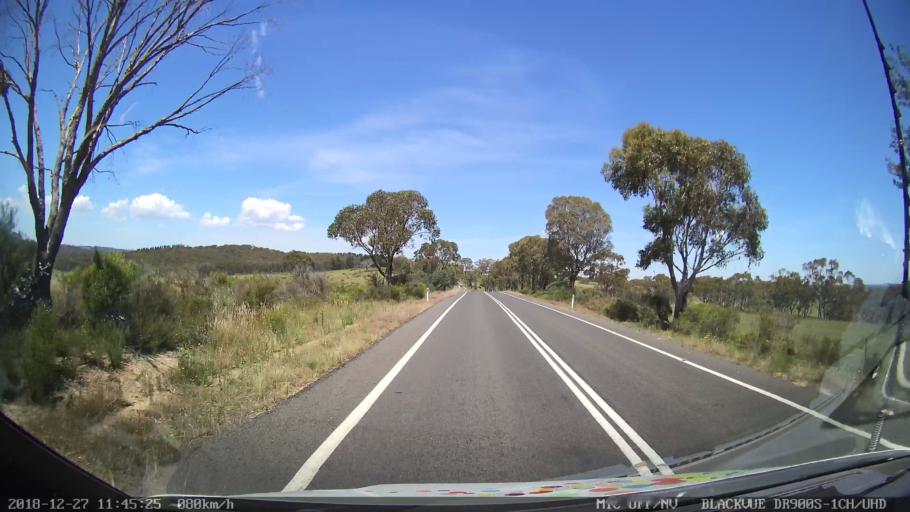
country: AU
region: New South Wales
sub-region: Bathurst Regional
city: Perthville
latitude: -33.5818
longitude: 149.4700
